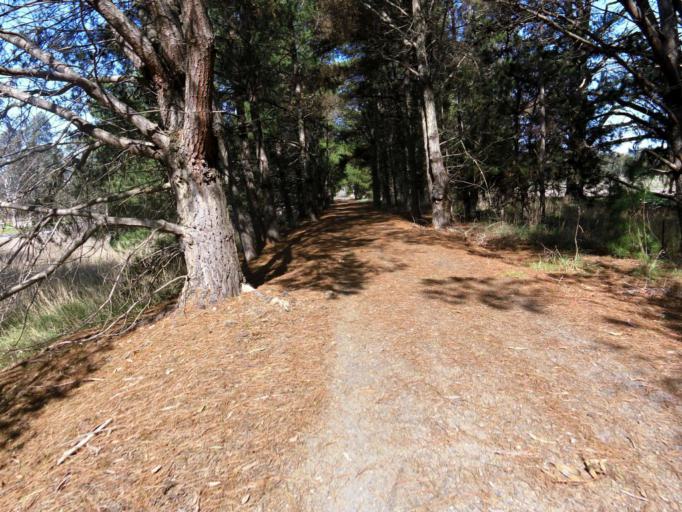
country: AU
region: Victoria
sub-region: Murrindindi
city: Alexandra
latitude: -36.9987
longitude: 145.7439
